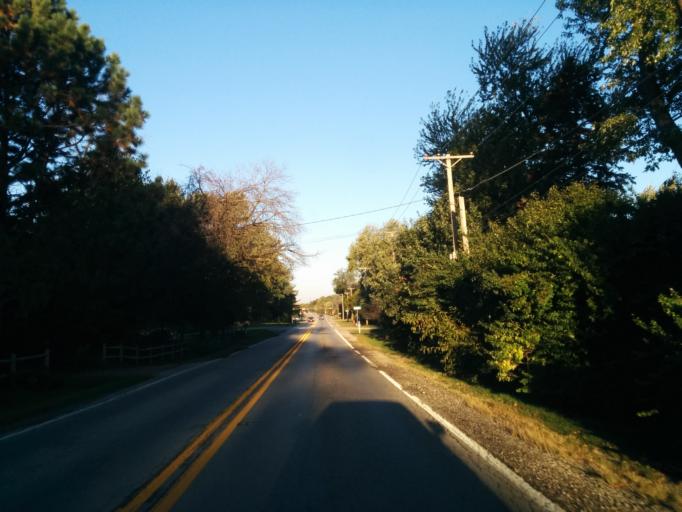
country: US
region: Illinois
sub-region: DuPage County
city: Glendale Heights
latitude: 41.8932
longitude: -88.0756
